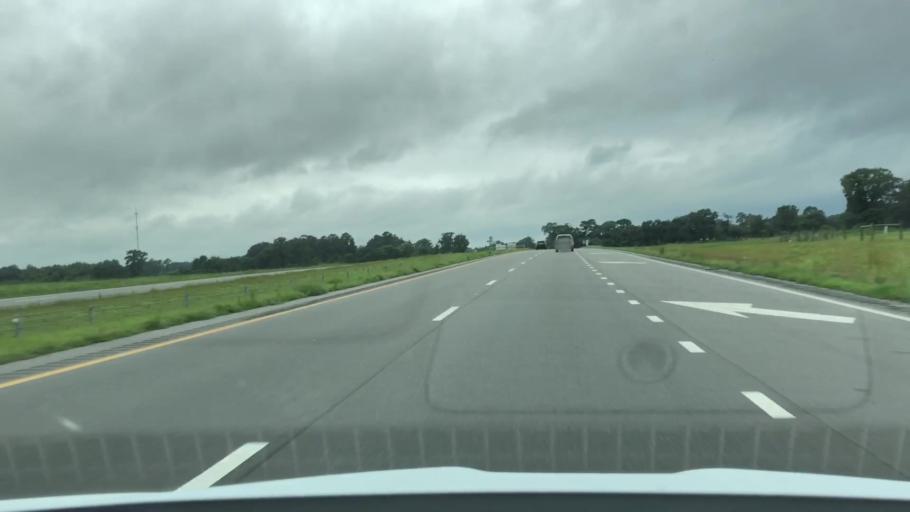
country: US
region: North Carolina
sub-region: Lenoir County
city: La Grange
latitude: 35.3044
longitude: -77.8190
